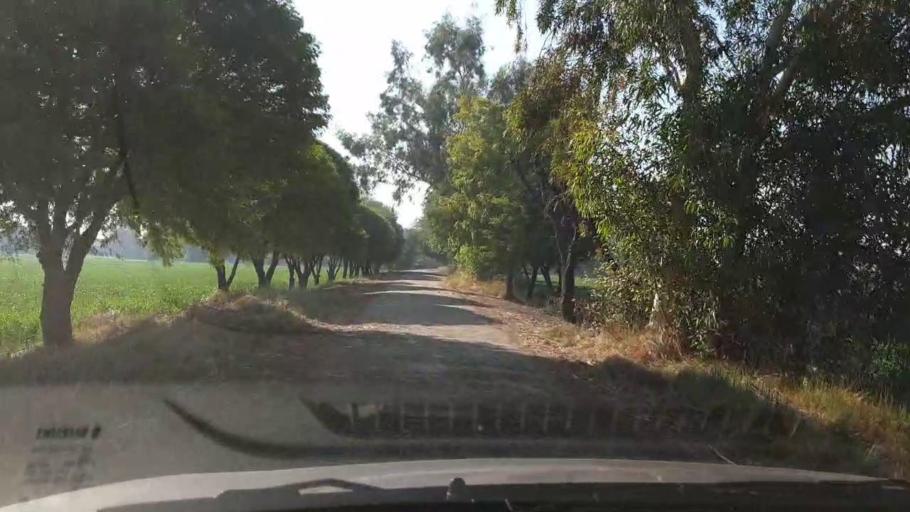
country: PK
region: Sindh
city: Jhol
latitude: 25.9447
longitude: 68.8474
